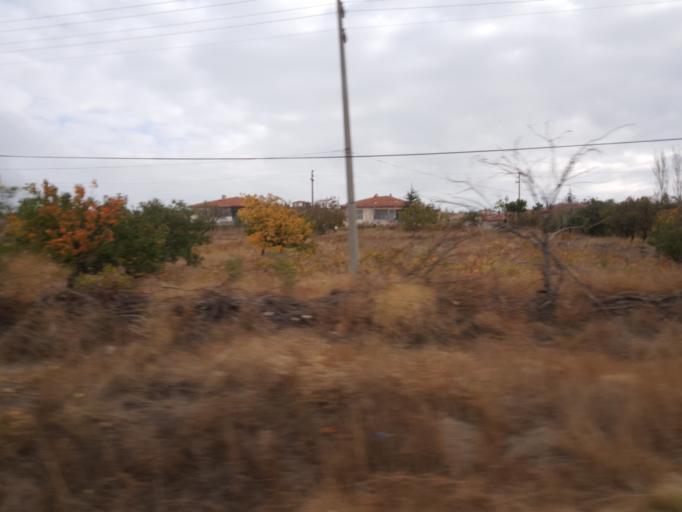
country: TR
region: Kirikkale
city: Keskin
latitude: 39.6788
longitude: 33.5987
